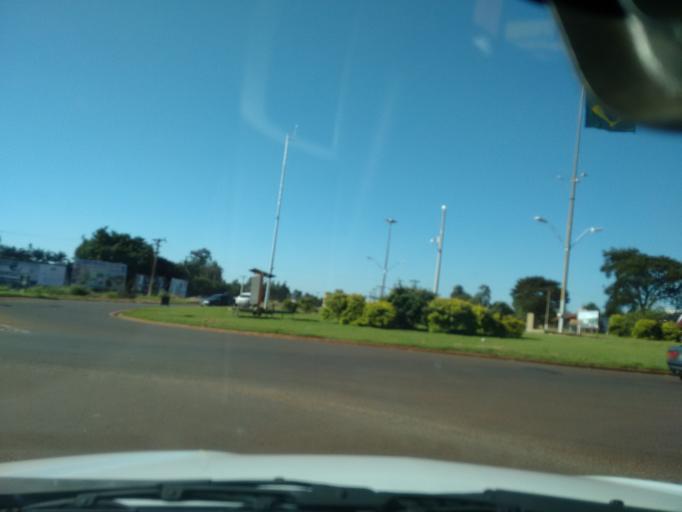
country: BR
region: Mato Grosso do Sul
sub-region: Dourados
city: Dourados
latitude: -22.2587
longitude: -54.8038
